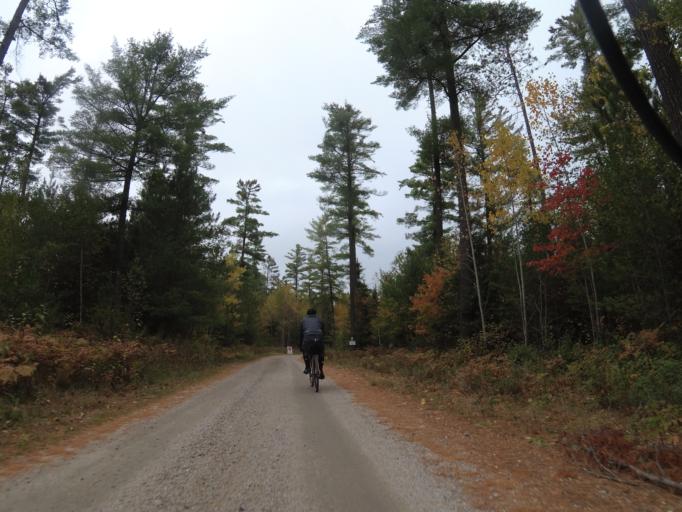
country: CA
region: Ontario
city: Renfrew
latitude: 45.2236
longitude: -77.0565
